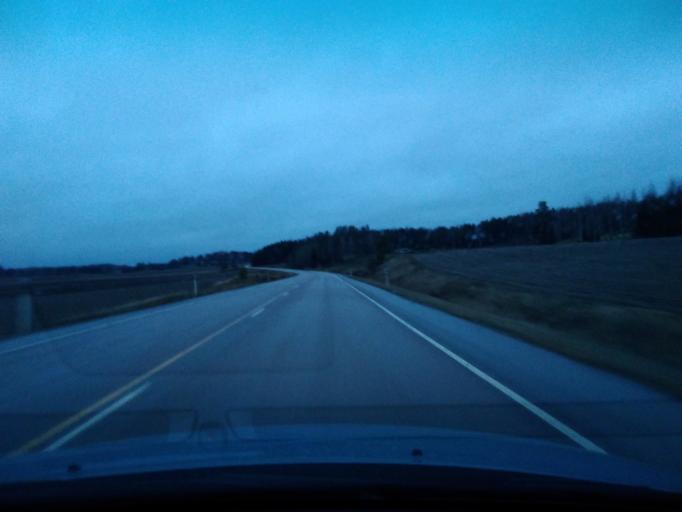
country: FI
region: Uusimaa
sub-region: Porvoo
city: Askola
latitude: 60.4801
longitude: 25.5641
